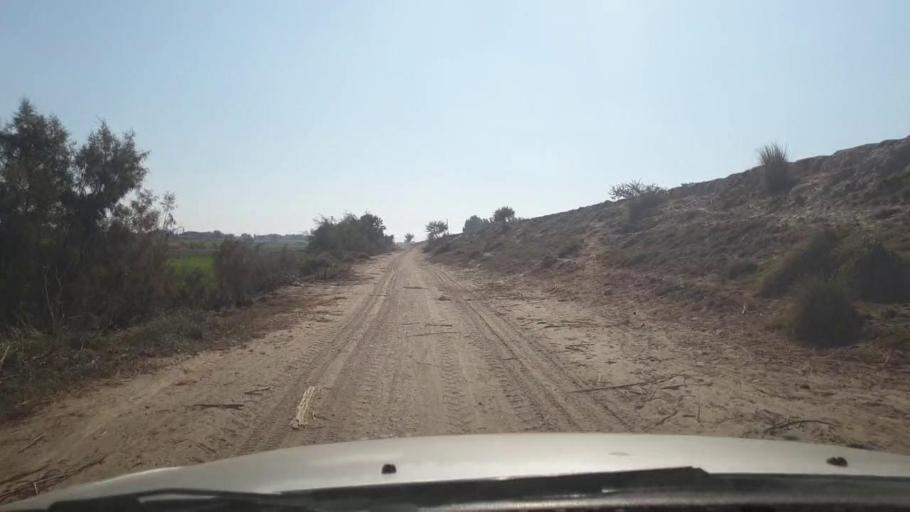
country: PK
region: Sindh
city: Ghotki
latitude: 28.0222
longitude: 69.2097
